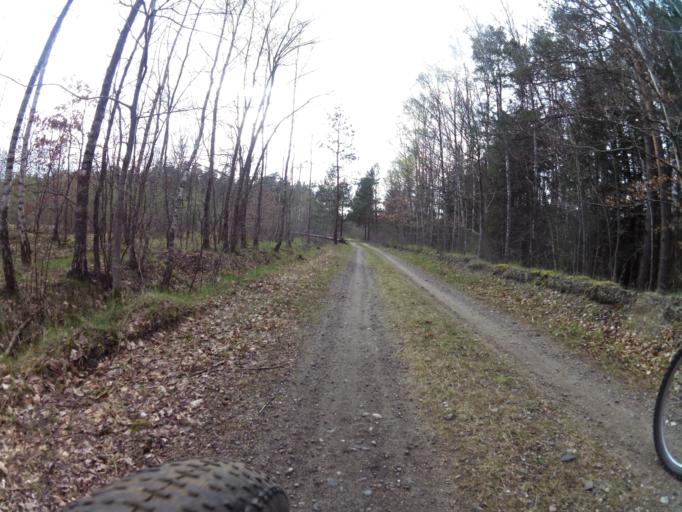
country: PL
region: West Pomeranian Voivodeship
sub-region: Powiat slawienski
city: Slawno
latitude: 54.3290
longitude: 16.7450
